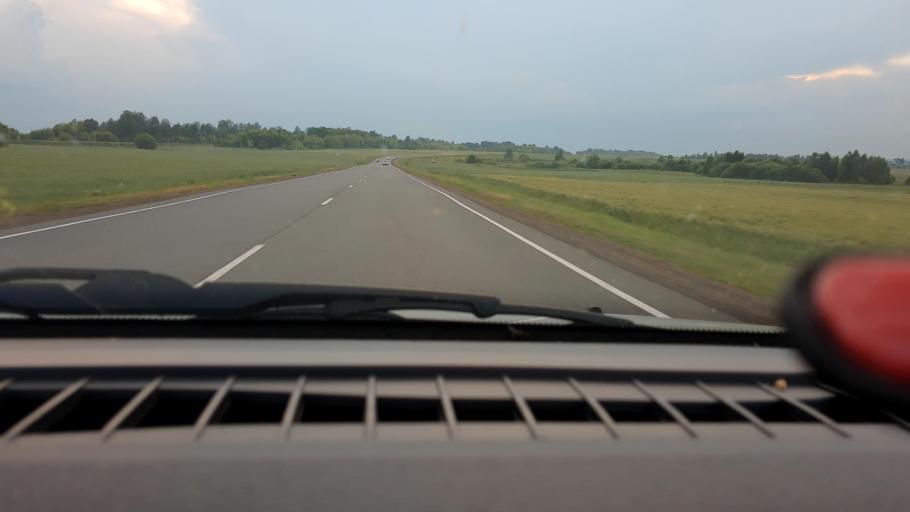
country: RU
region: Nizjnij Novgorod
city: Shatki
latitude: 55.2498
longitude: 43.9938
